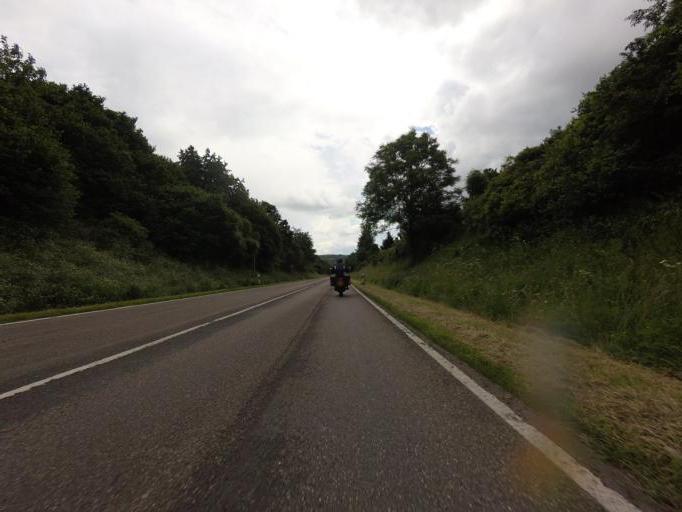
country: DE
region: Rheinland-Pfalz
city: Kaisersesch
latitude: 50.2321
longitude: 7.1465
